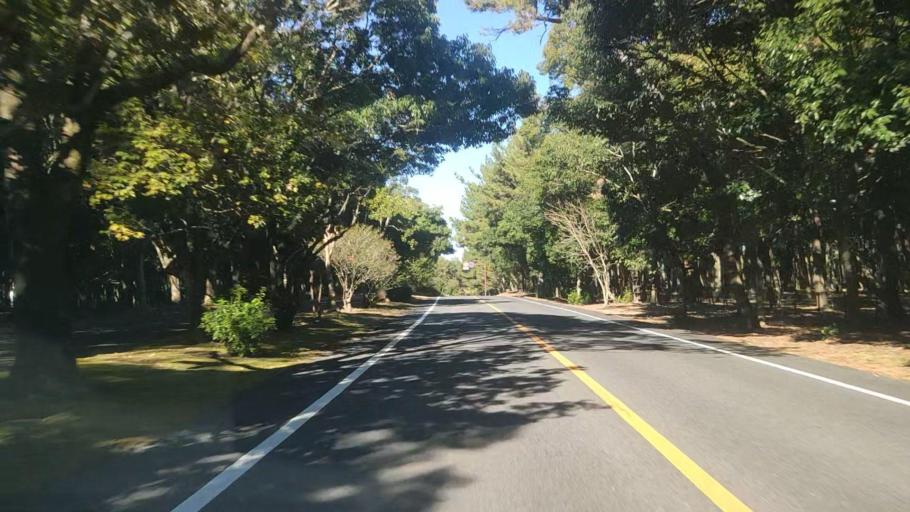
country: JP
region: Miyazaki
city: Miyazaki-shi
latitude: 31.9439
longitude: 131.4648
